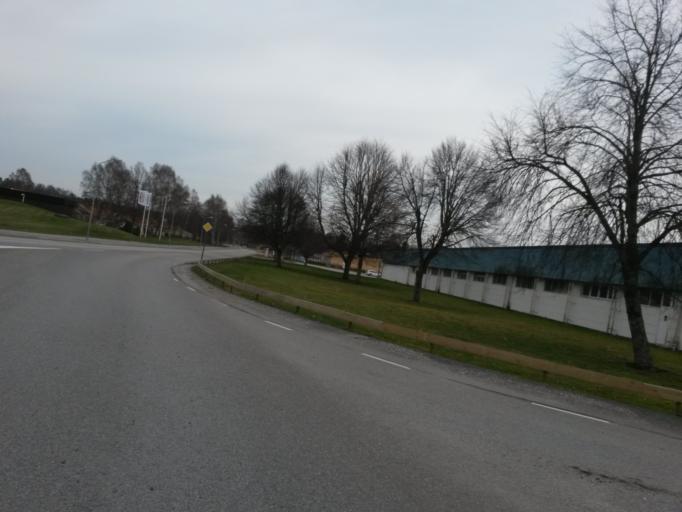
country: SE
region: Vaestra Goetaland
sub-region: Herrljunga Kommun
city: Herrljunga
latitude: 58.0744
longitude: 13.0200
